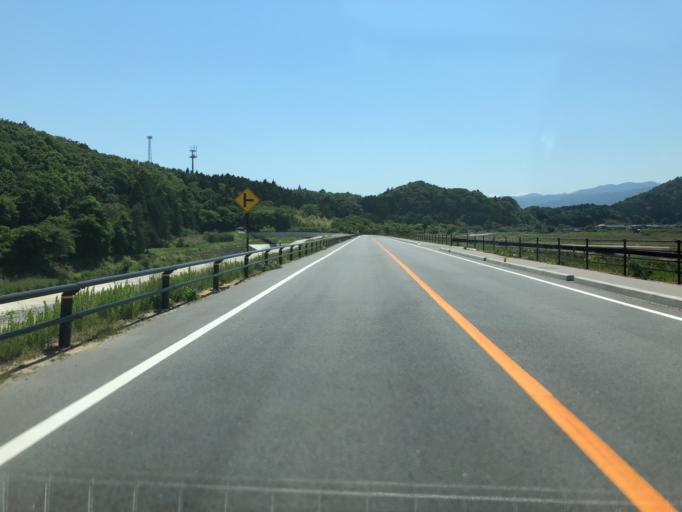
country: JP
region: Fukushima
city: Iwaki
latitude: 37.2076
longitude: 141.0021
